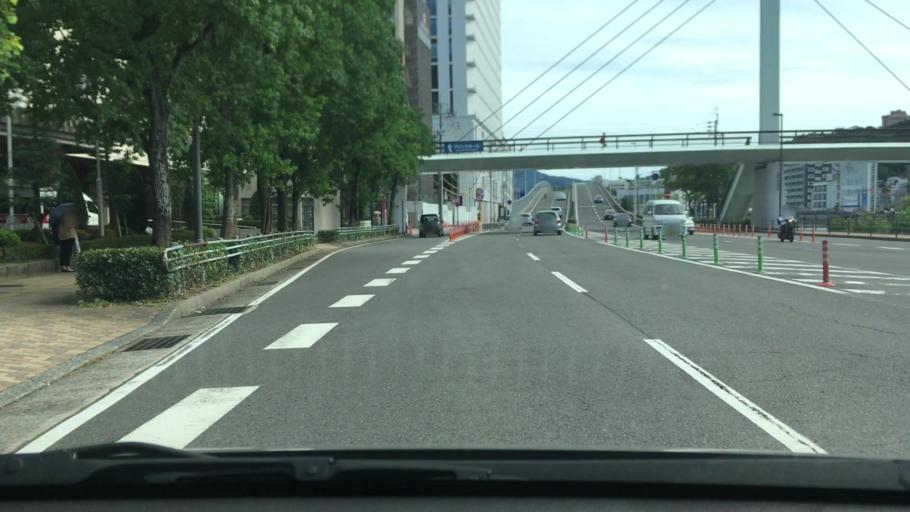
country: JP
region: Nagasaki
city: Nagasaki-shi
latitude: 32.7665
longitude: 129.8623
